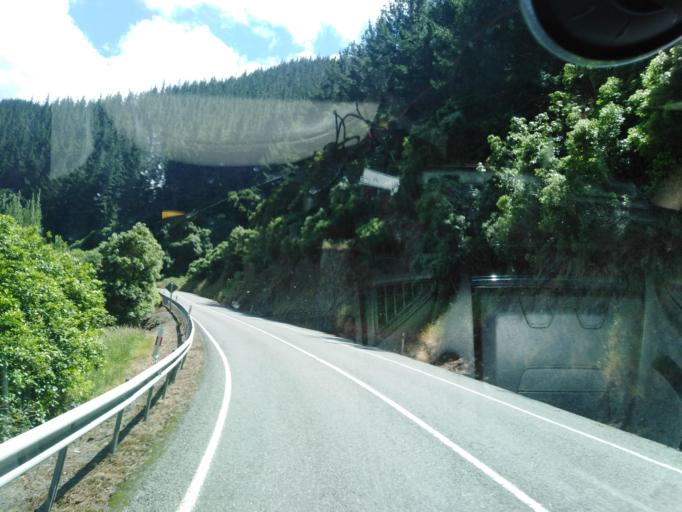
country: NZ
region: Nelson
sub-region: Nelson City
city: Nelson
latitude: -41.2296
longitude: 173.4118
